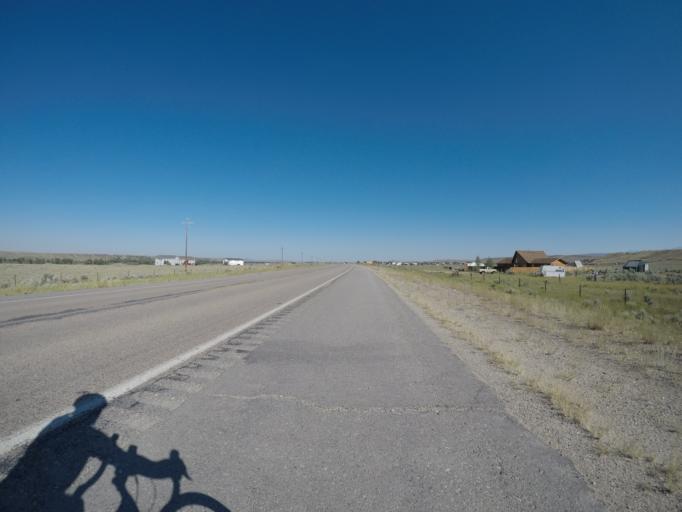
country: US
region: Wyoming
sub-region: Sublette County
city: Pinedale
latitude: 42.7619
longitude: -109.7356
